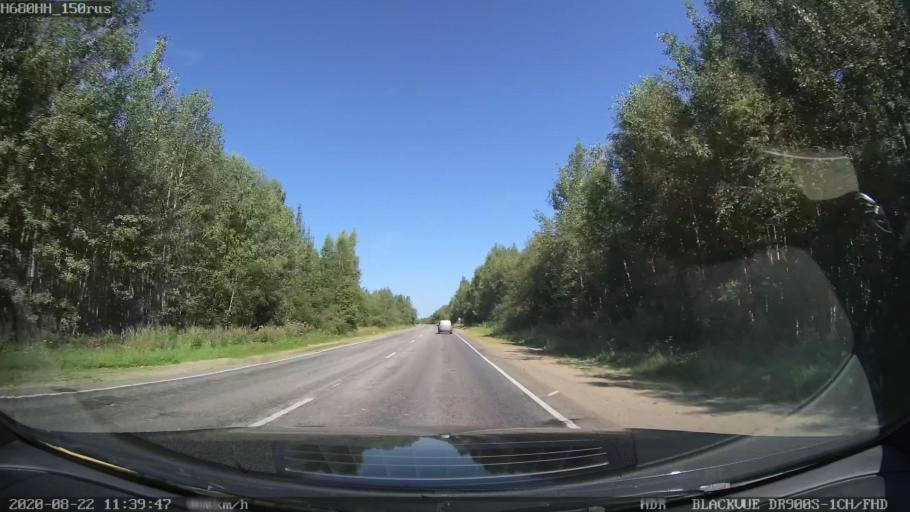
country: RU
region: Tverskaya
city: Sakharovo
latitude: 56.9690
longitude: 36.0229
